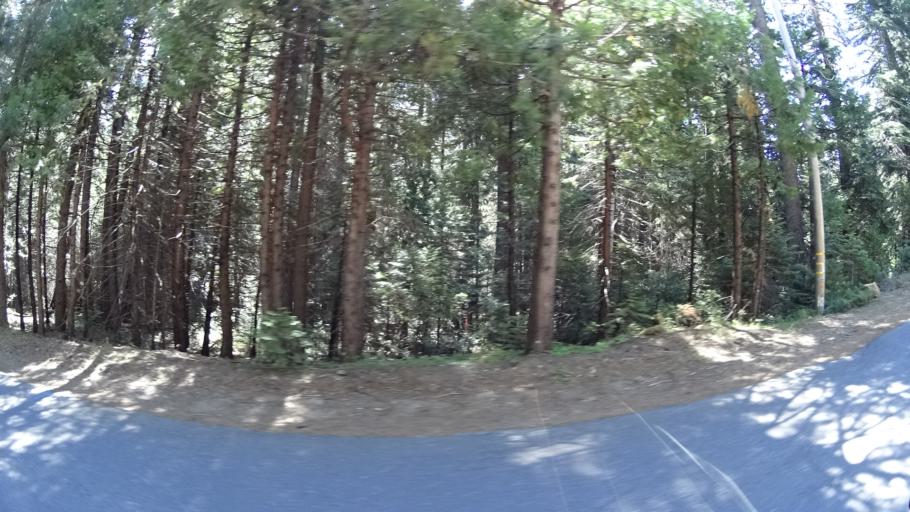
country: US
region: California
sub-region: Calaveras County
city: Arnold
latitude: 38.2966
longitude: -120.2756
